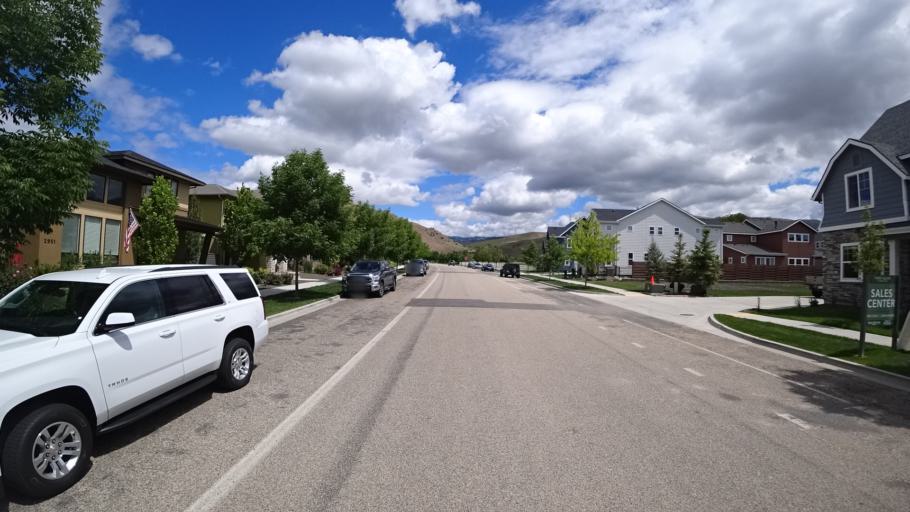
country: US
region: Idaho
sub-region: Ada County
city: Boise
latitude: 43.5763
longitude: -116.1325
